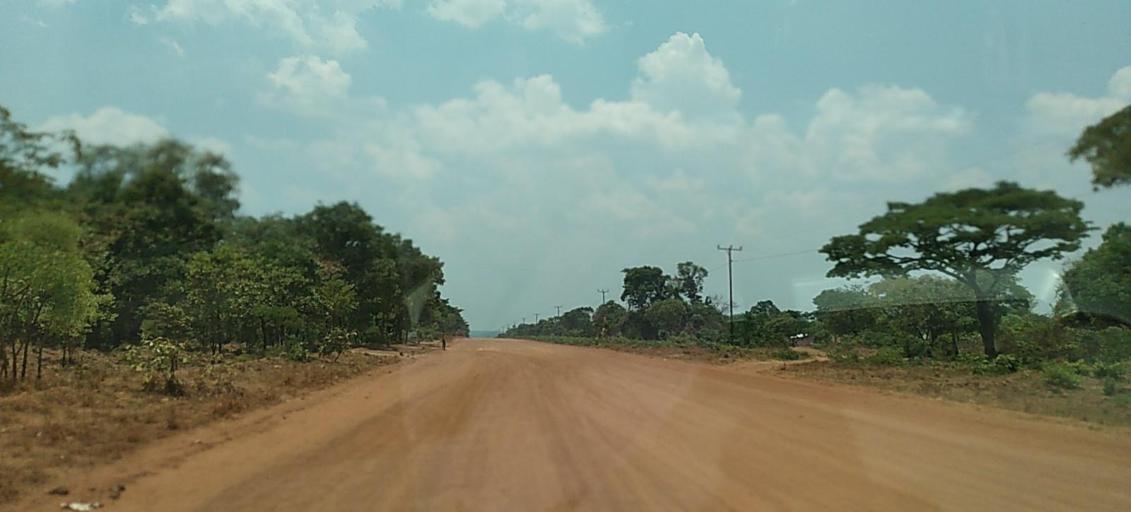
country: ZM
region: Copperbelt
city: Chingola
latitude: -12.8920
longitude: 27.5801
